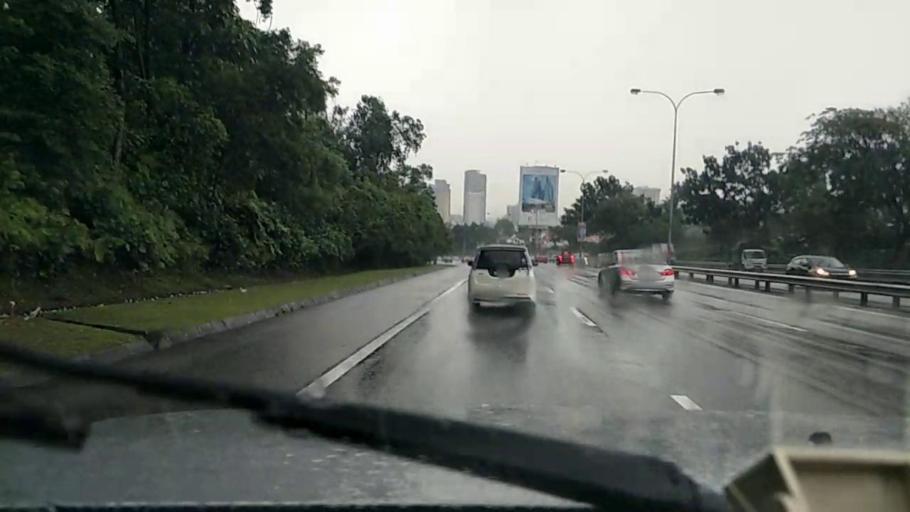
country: MY
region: Kuala Lumpur
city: Kuala Lumpur
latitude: 3.1107
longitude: 101.6889
